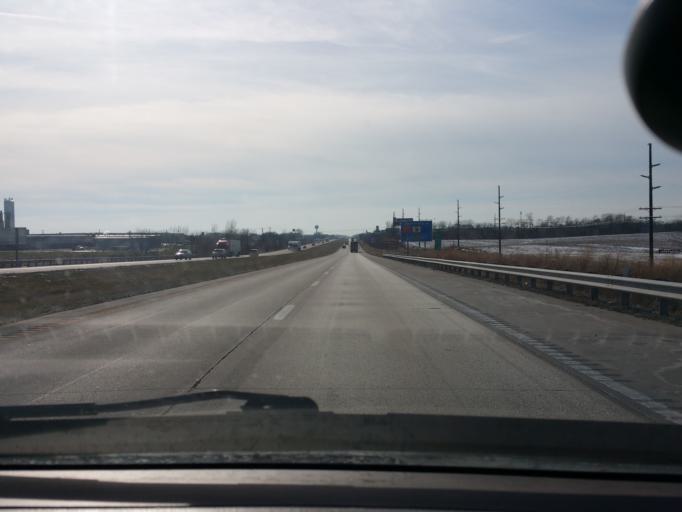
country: US
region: Missouri
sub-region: Clay County
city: Kearney
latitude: 39.3795
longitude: -94.3662
